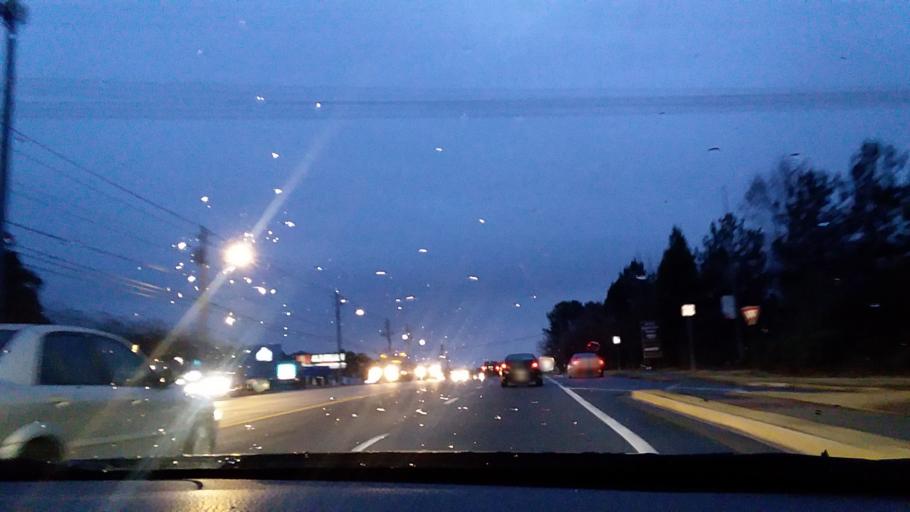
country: US
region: Georgia
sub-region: DeKalb County
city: Tucker
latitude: 33.8723
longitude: -84.1880
